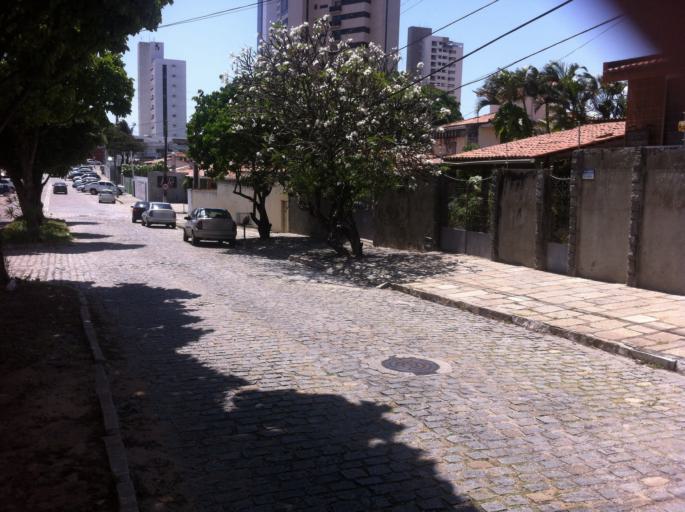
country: BR
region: Rio Grande do Norte
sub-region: Natal
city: Natal
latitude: -5.8203
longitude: -35.2142
